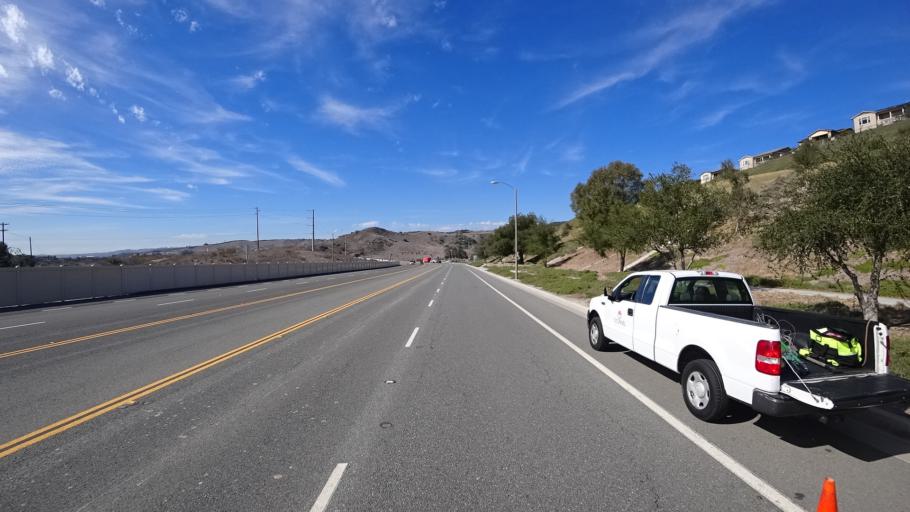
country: US
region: California
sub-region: Orange County
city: Ladera Ranch
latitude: 33.5286
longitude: -117.6032
